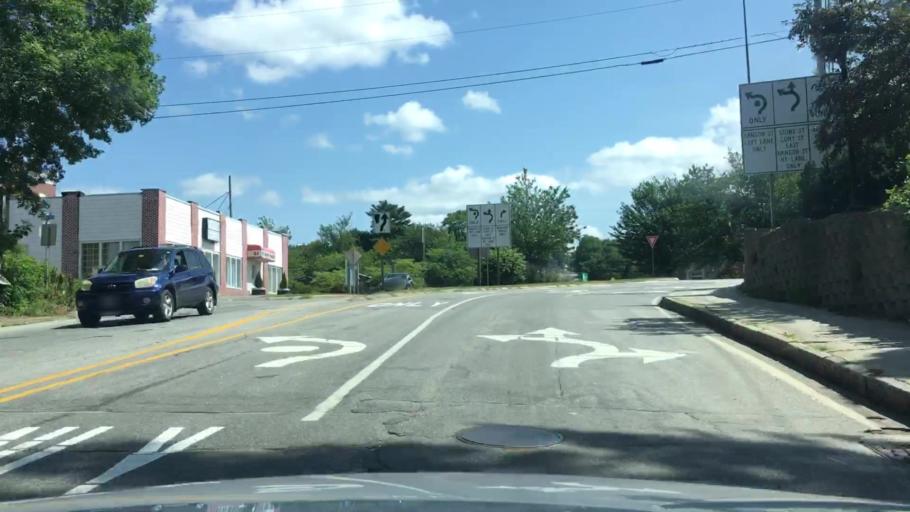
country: US
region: Maine
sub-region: Kennebec County
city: Augusta
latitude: 44.3165
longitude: -69.7691
